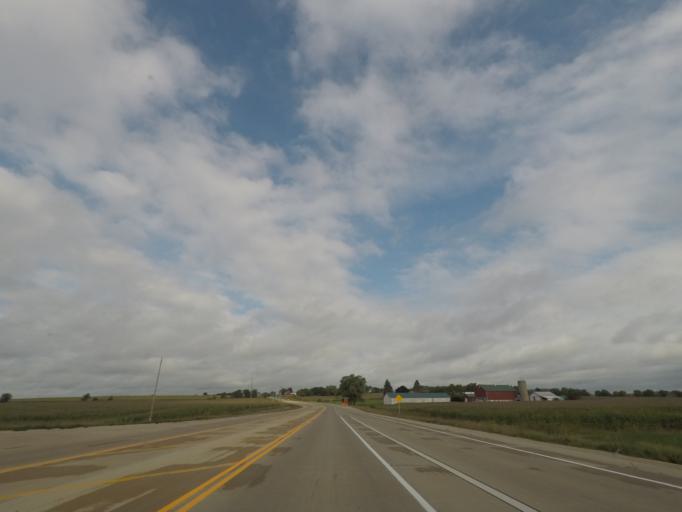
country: US
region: Wisconsin
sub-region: Dane County
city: Deerfield
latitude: 43.0302
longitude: -89.0819
